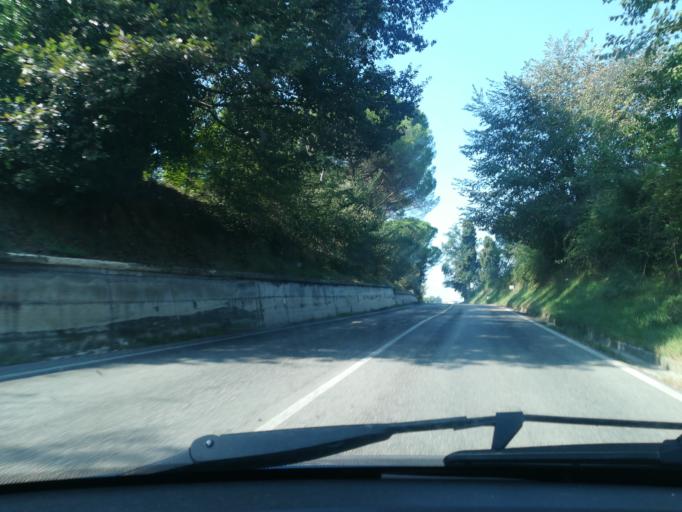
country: IT
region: The Marches
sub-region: Provincia di Macerata
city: Piediripa
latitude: 43.2692
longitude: 13.4688
